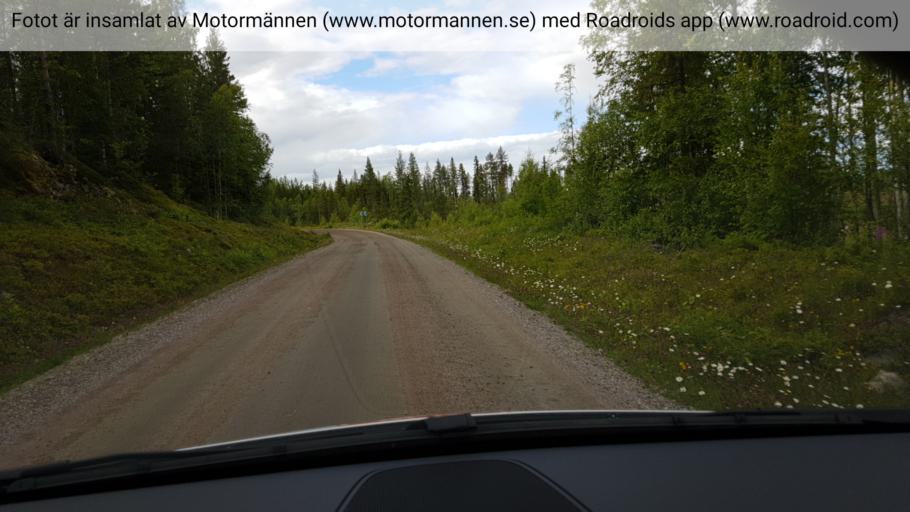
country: SE
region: Vaesterbotten
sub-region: Dorotea Kommun
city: Dorotea
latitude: 63.9314
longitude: 16.1584
